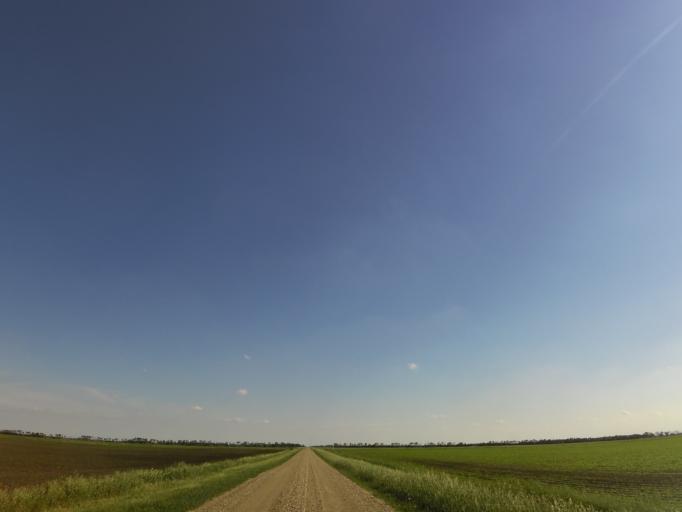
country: US
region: North Dakota
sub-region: Walsh County
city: Grafton
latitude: 48.3419
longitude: -97.2329
